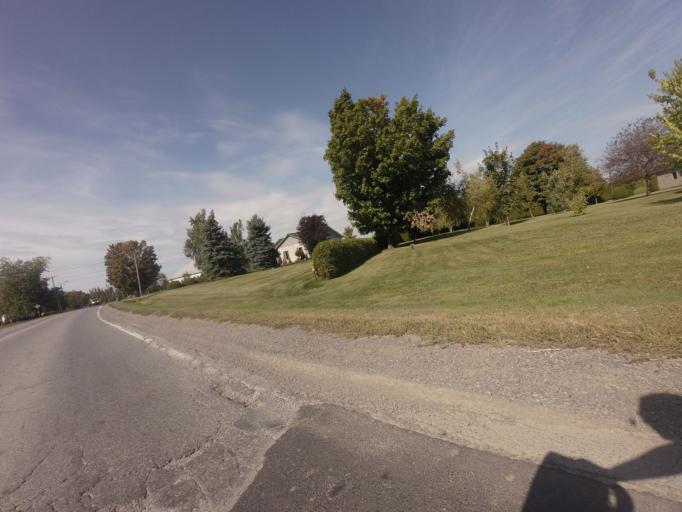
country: CA
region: Quebec
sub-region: Laurentides
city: Saint-Eustache
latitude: 45.5937
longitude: -73.9094
